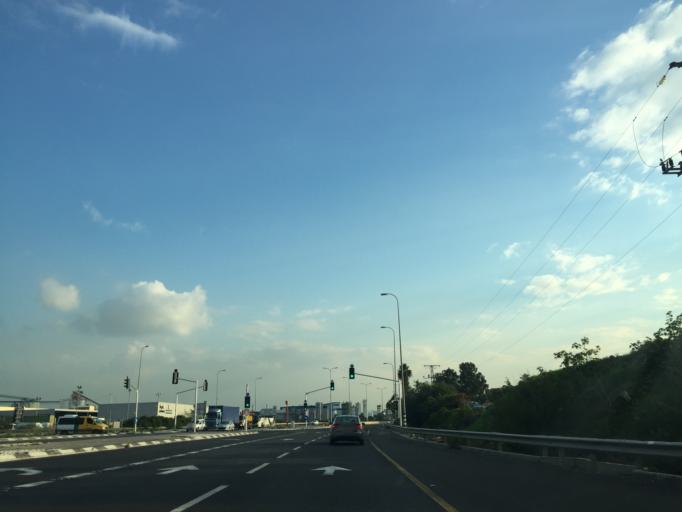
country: IL
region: Central District
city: Ramla
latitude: 31.9234
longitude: 34.8842
